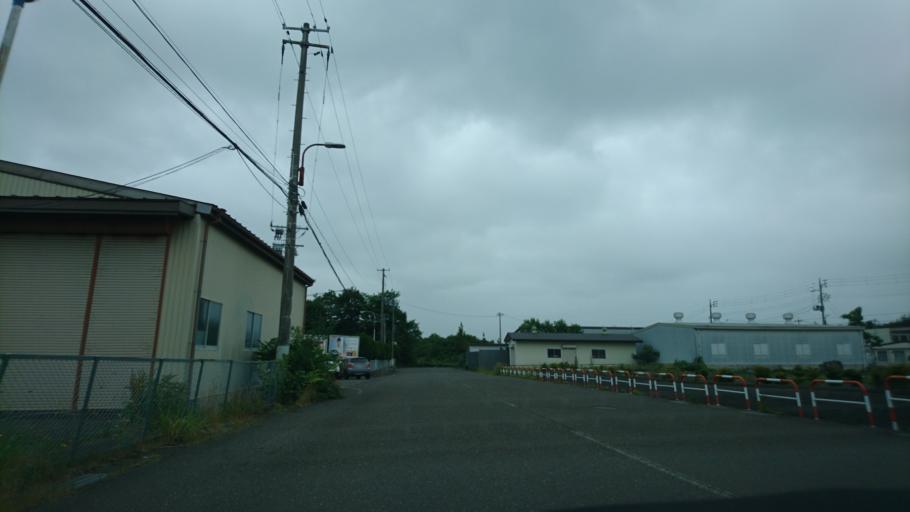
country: JP
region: Iwate
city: Ichinoseki
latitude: 38.9056
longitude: 141.1600
